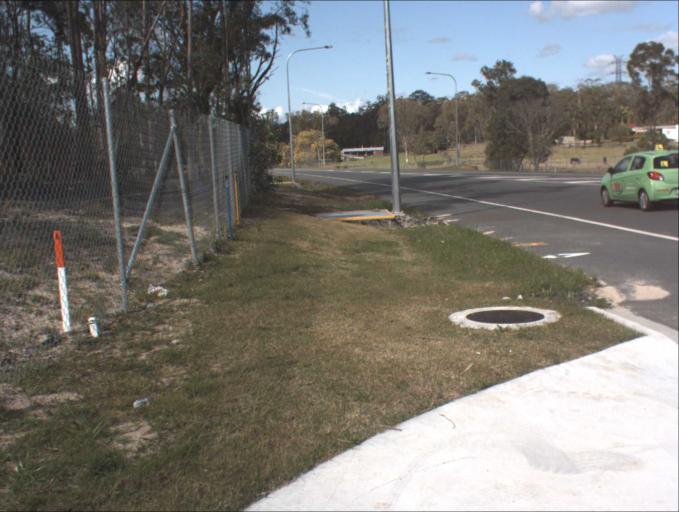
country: AU
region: Queensland
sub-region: Logan
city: Logan Reserve
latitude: -27.6895
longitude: 153.0695
